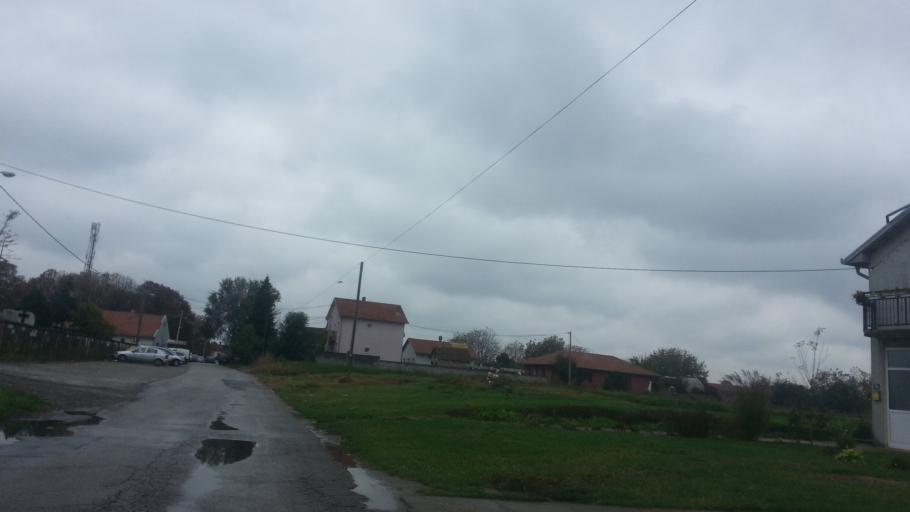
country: RS
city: Novi Banovci
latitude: 44.9081
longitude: 20.2810
